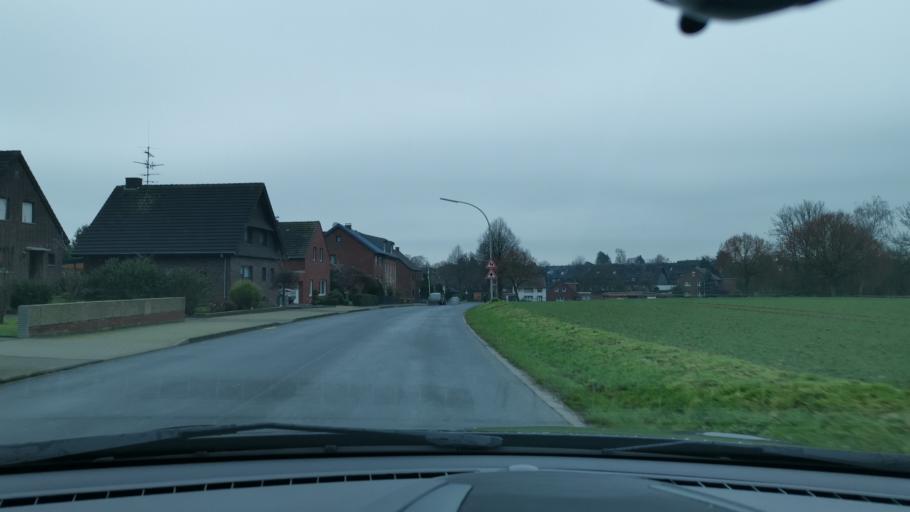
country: DE
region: North Rhine-Westphalia
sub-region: Regierungsbezirk Dusseldorf
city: Juchen
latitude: 51.1160
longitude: 6.5405
